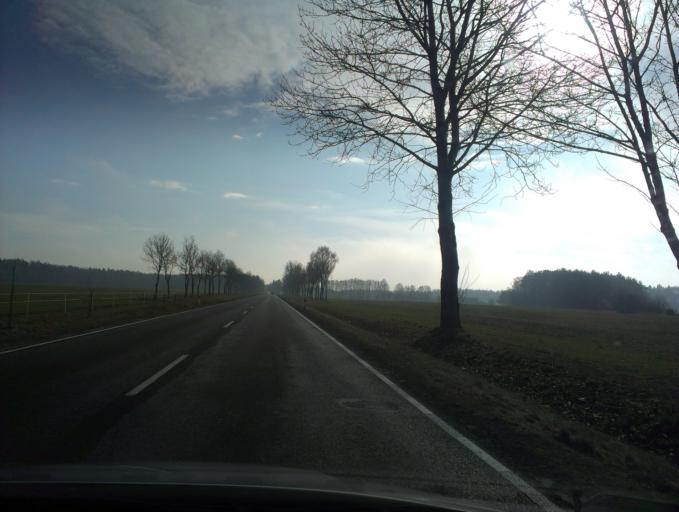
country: PL
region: West Pomeranian Voivodeship
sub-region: Powiat koszalinski
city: Bobolice
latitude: 54.0190
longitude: 16.4844
